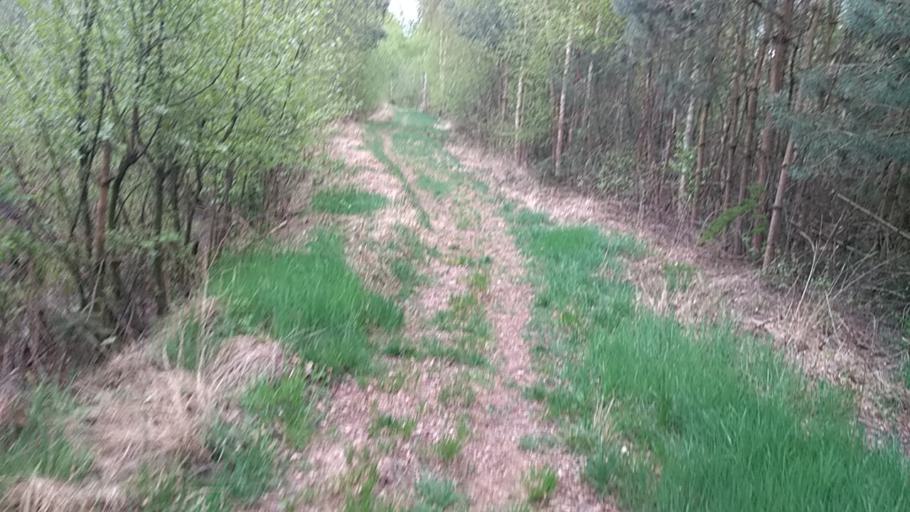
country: NL
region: Limburg
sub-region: Gemeente Leudal
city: Heythuysen
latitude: 51.2959
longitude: 5.8449
